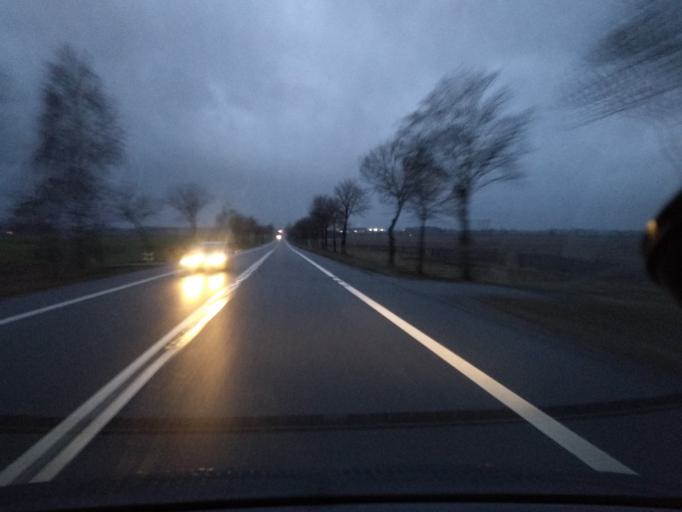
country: PL
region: Lower Silesian Voivodeship
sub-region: Powiat sredzki
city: Miekinia
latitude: 51.1612
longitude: 16.6975
